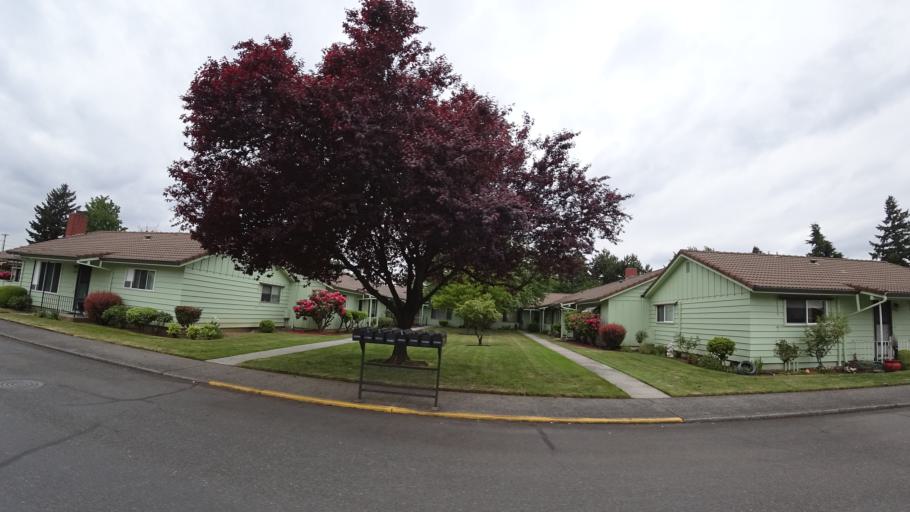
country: US
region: Oregon
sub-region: Multnomah County
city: Lents
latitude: 45.5138
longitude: -122.5361
